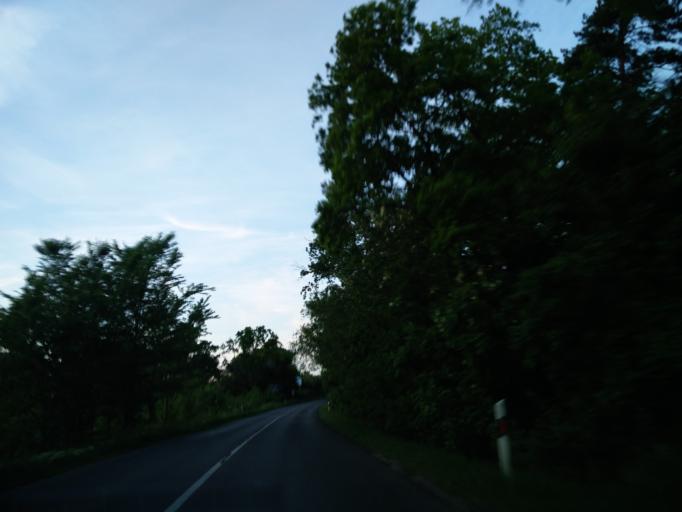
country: HU
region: Pest
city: Budakeszi
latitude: 47.4757
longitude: 18.9025
